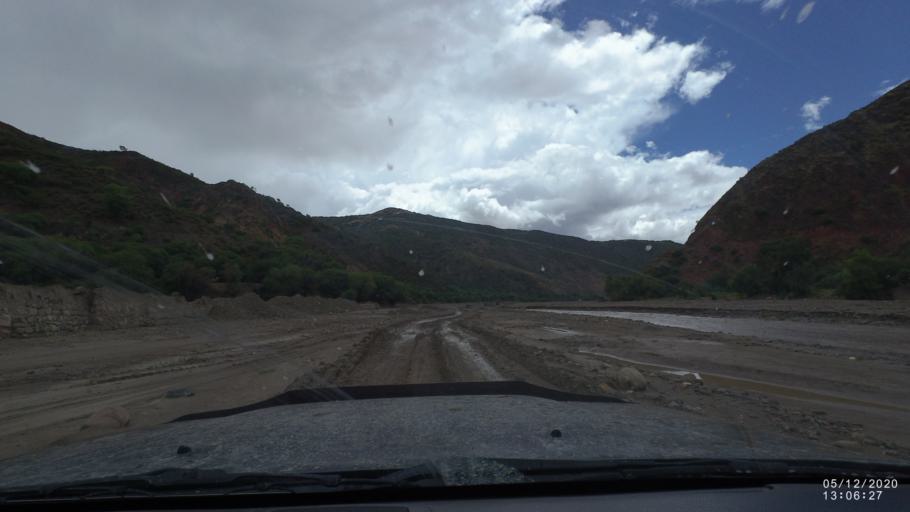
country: BO
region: Cochabamba
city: Sipe Sipe
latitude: -17.5584
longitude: -66.4450
